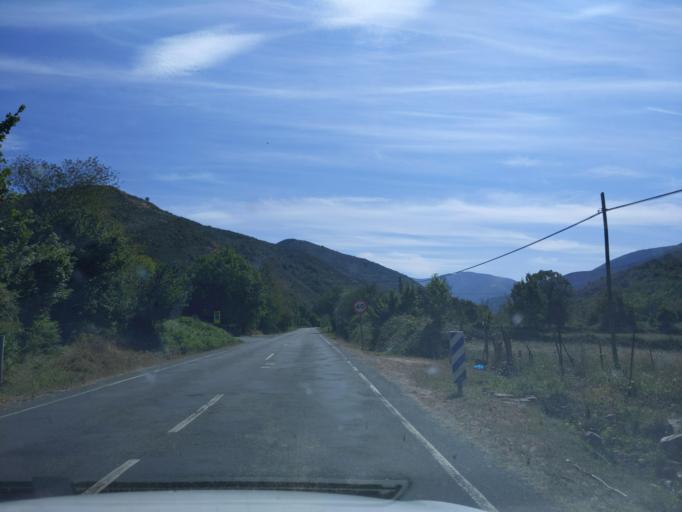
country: ES
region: La Rioja
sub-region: Provincia de La Rioja
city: Ezcaray
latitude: 42.2963
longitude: -3.0251
